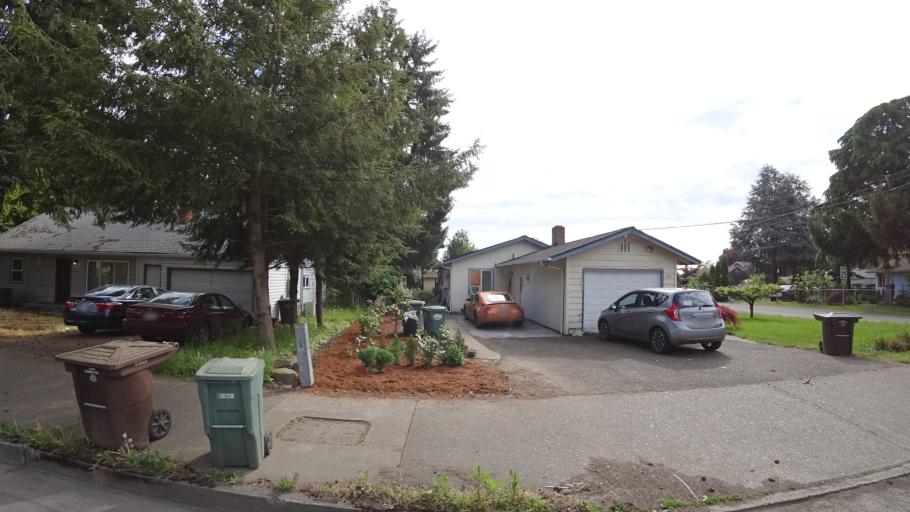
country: US
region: Oregon
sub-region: Washington County
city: Hillsboro
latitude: 45.5047
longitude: -122.9635
